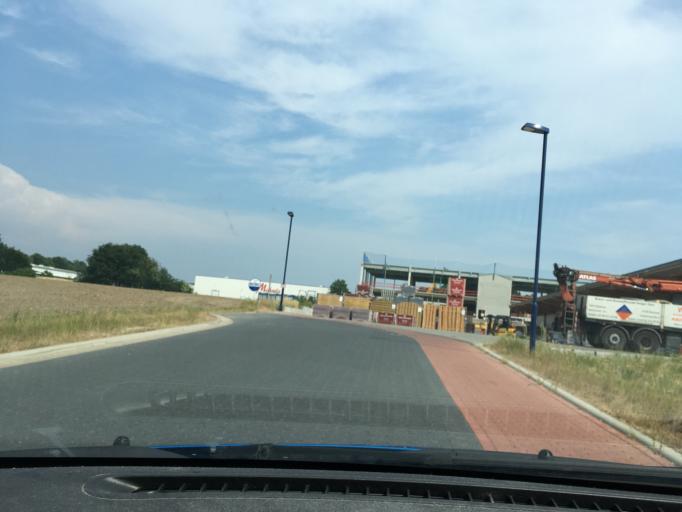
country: DE
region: Lower Saxony
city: Salzhausen
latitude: 53.2284
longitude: 10.1458
